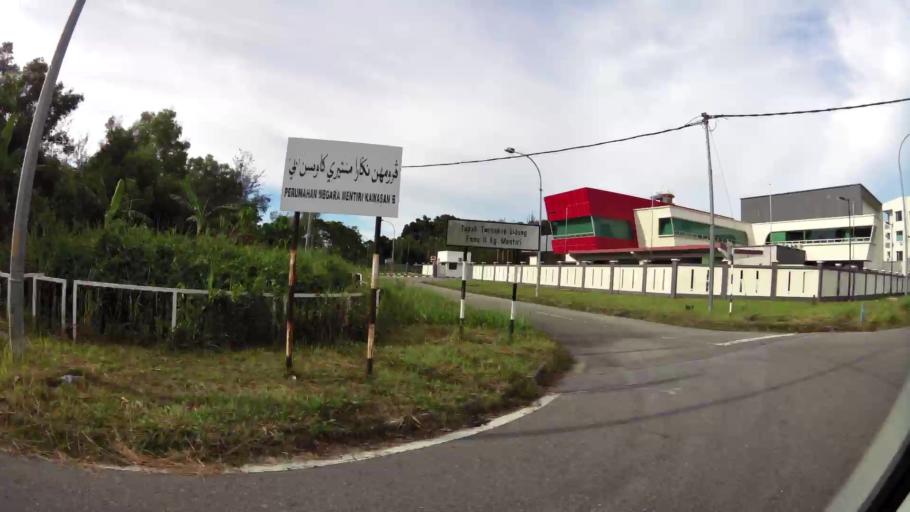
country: BN
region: Brunei and Muara
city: Bandar Seri Begawan
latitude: 4.9723
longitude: 115.0326
